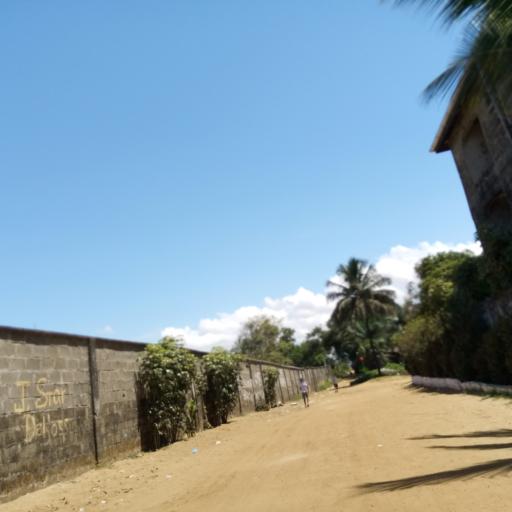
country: LR
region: Montserrado
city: Monrovia
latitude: 6.2362
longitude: -10.6956
